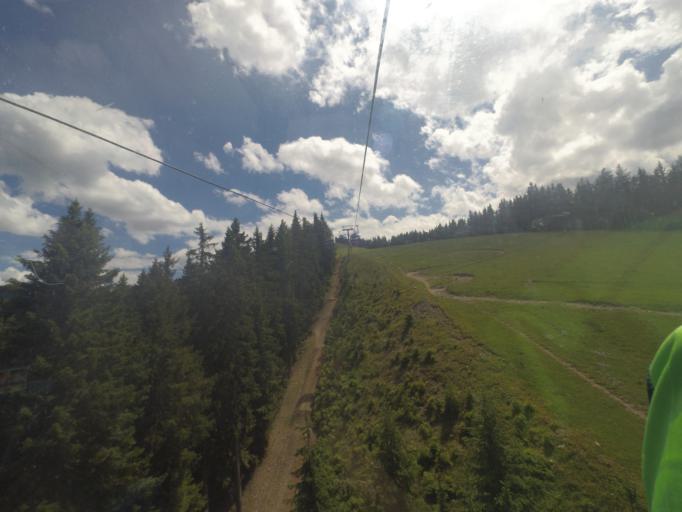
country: AT
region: Salzburg
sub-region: Politischer Bezirk Zell am See
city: Leogang
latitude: 47.4223
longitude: 12.7141
